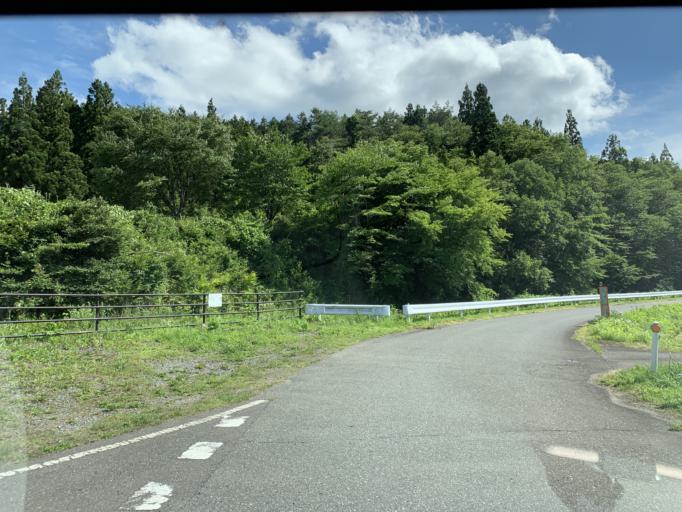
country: JP
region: Iwate
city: Ichinoseki
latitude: 38.9619
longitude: 140.9521
